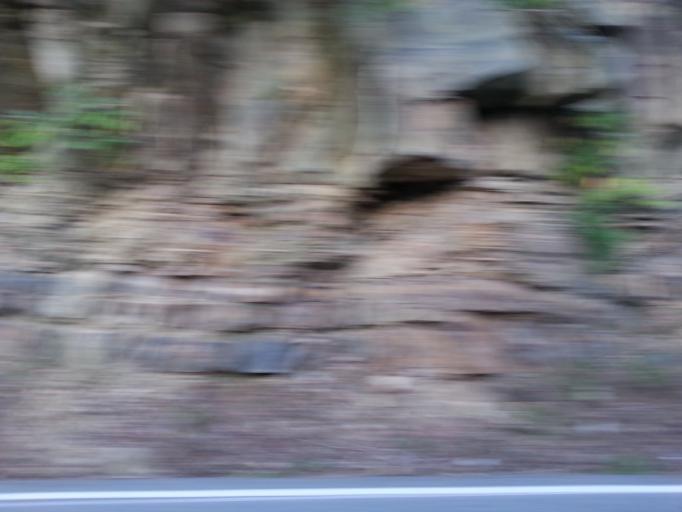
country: US
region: Tennessee
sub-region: Johnson County
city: Mountain City
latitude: 36.4765
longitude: -81.9748
